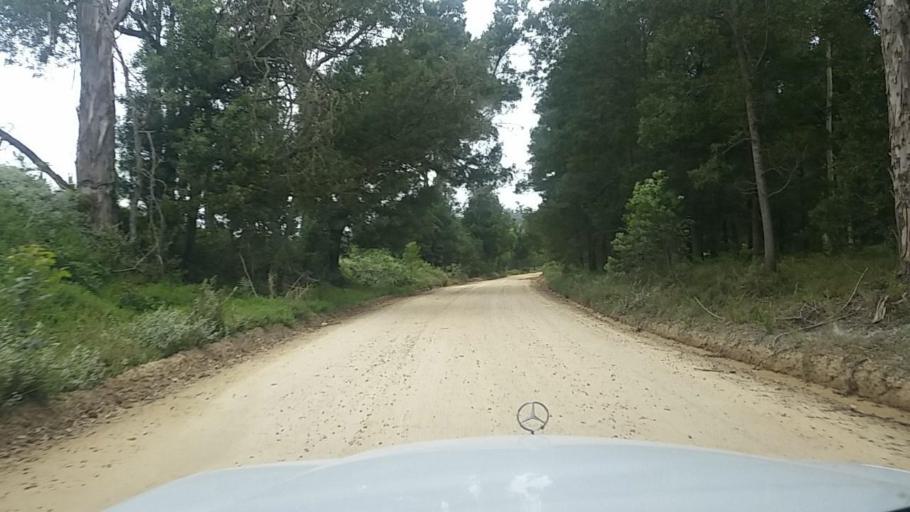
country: ZA
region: Western Cape
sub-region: Eden District Municipality
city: Knysna
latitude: -33.9879
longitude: 23.1475
